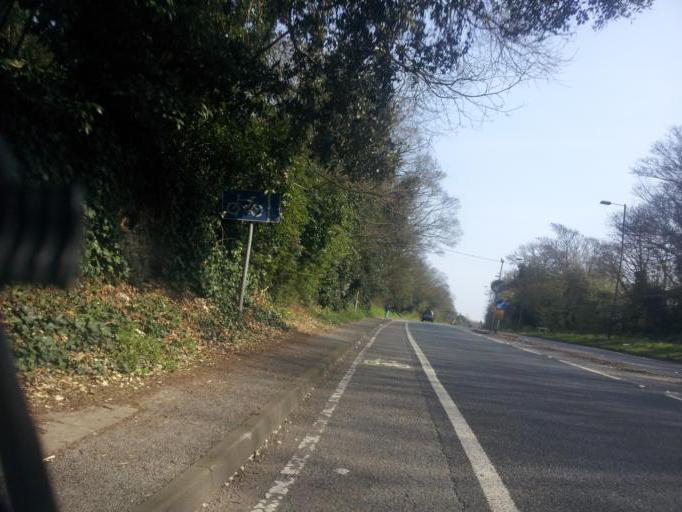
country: GB
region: England
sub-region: Kent
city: Strood
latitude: 51.4078
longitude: 0.4724
